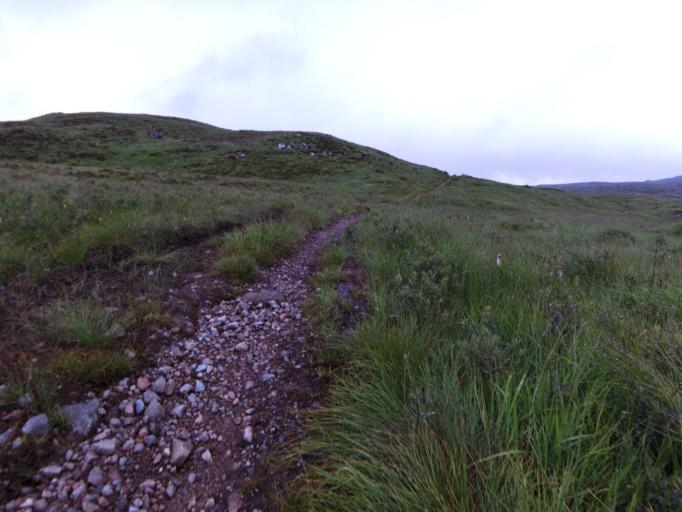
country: GB
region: Scotland
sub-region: Highland
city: Spean Bridge
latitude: 56.7663
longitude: -4.7020
